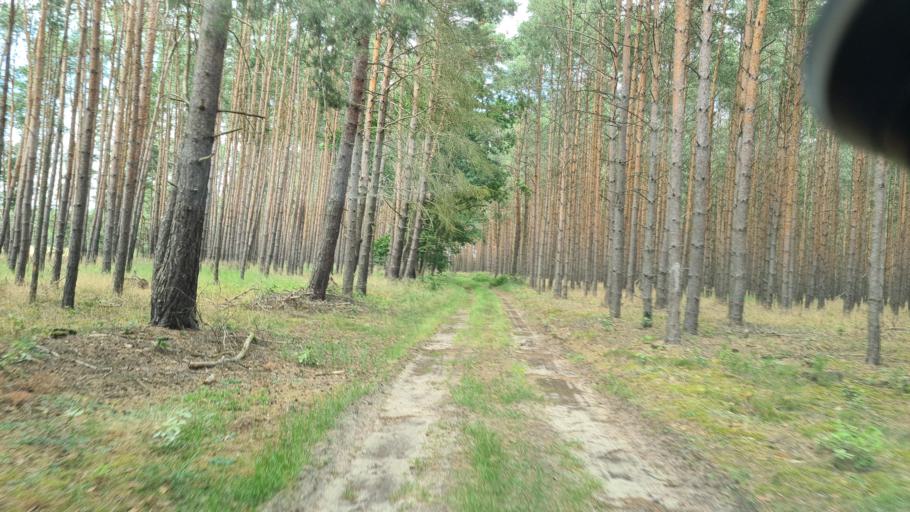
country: DE
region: Brandenburg
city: Sonnewalde
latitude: 51.6549
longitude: 13.6578
